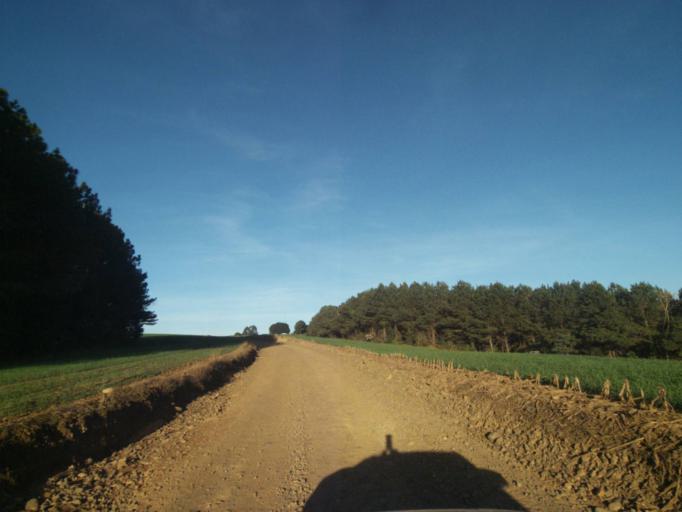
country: BR
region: Parana
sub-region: Telemaco Borba
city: Telemaco Borba
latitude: -24.4705
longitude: -50.5916
